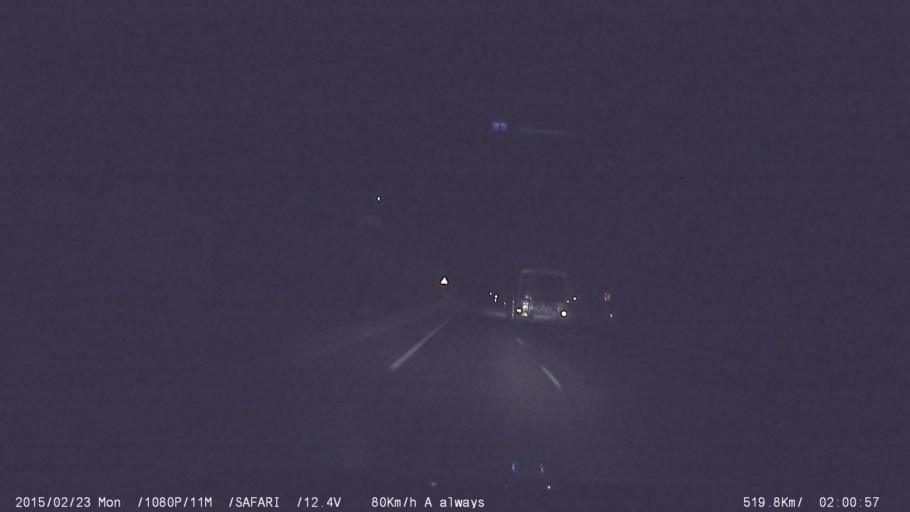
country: IN
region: Tamil Nadu
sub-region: Krishnagiri
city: Krishnagiri
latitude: 12.6279
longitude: 78.0780
